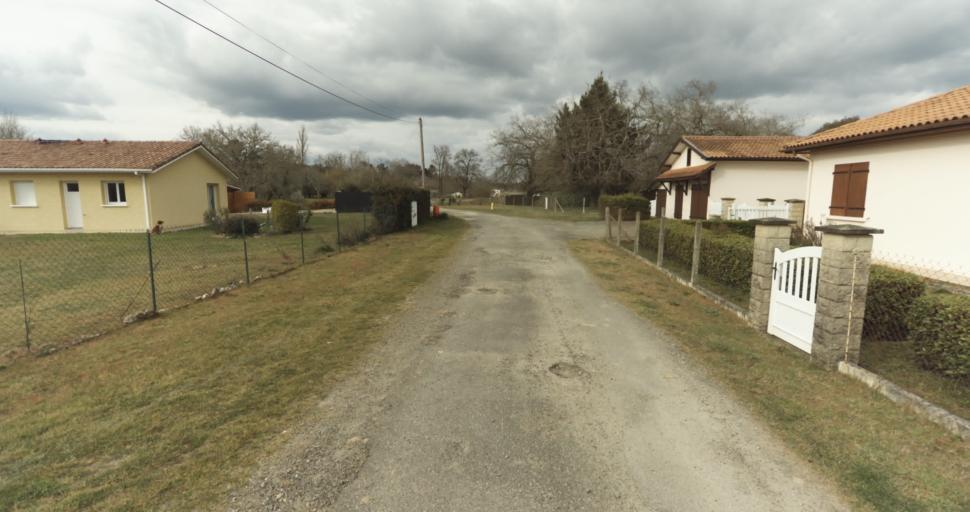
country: FR
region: Aquitaine
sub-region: Departement des Landes
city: Roquefort
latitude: 44.0415
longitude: -0.3282
